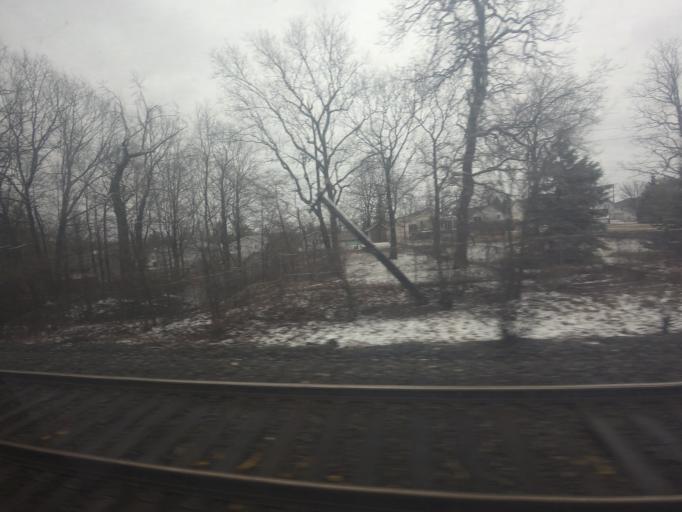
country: CA
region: Ontario
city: Kingston
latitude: 44.2278
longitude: -76.6567
